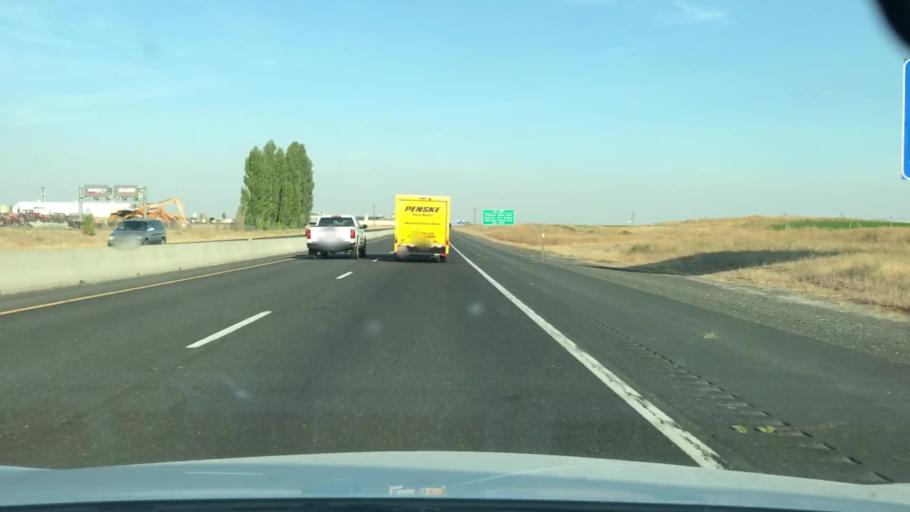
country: US
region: Washington
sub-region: Grant County
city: Moses Lake
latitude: 47.1006
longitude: -119.2610
